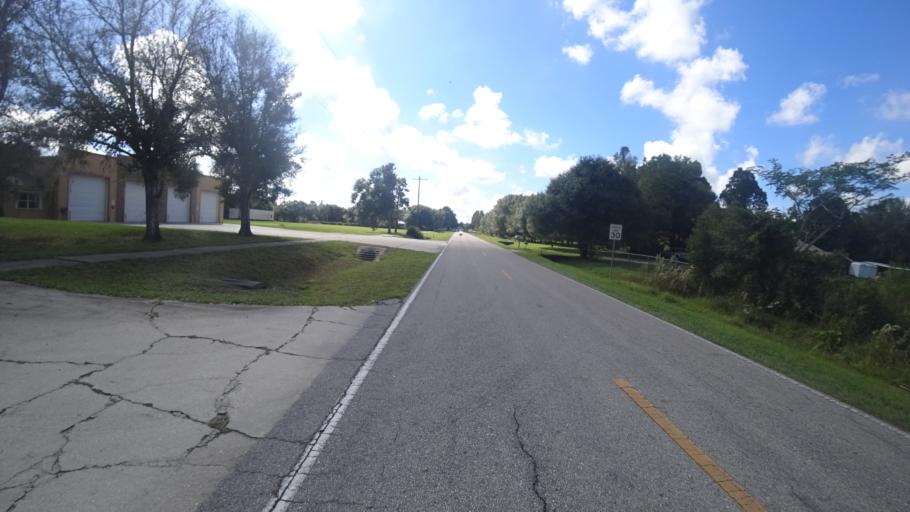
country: US
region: Florida
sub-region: Sarasota County
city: Lake Sarasota
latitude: 27.3553
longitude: -82.1625
